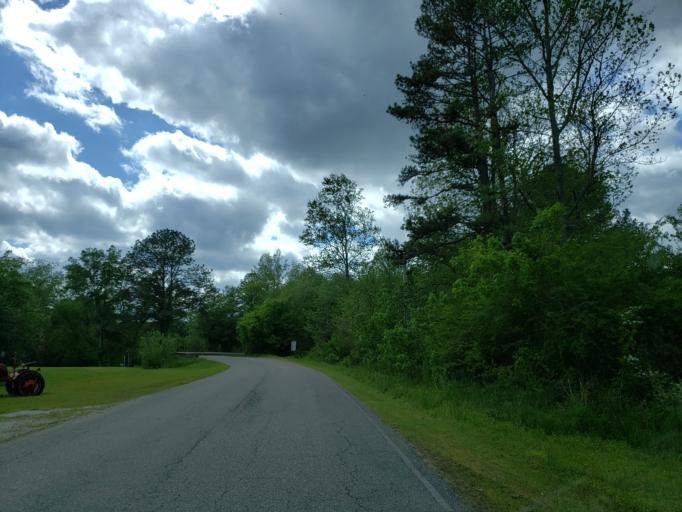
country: US
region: Georgia
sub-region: Haralson County
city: Tallapoosa
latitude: 33.7303
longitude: -85.3874
